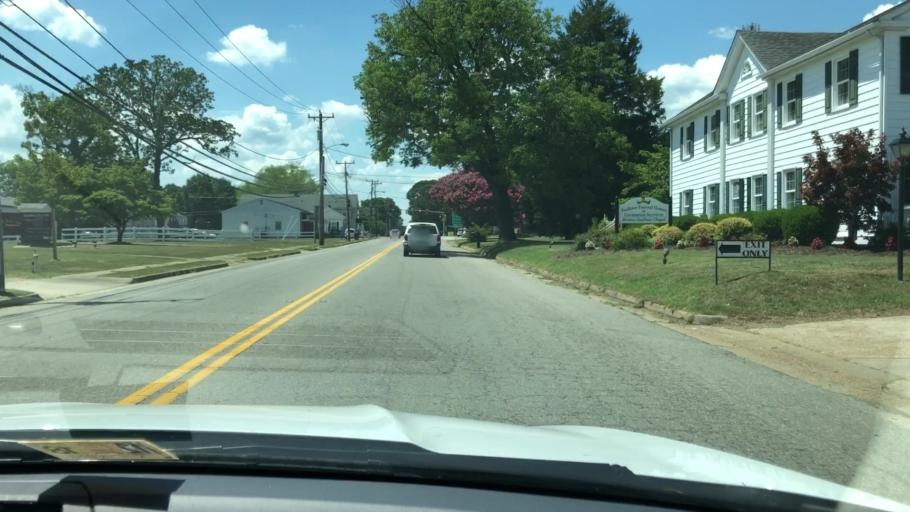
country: US
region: Virginia
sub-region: Middlesex County
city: Saluda
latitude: 37.6055
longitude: -76.5929
